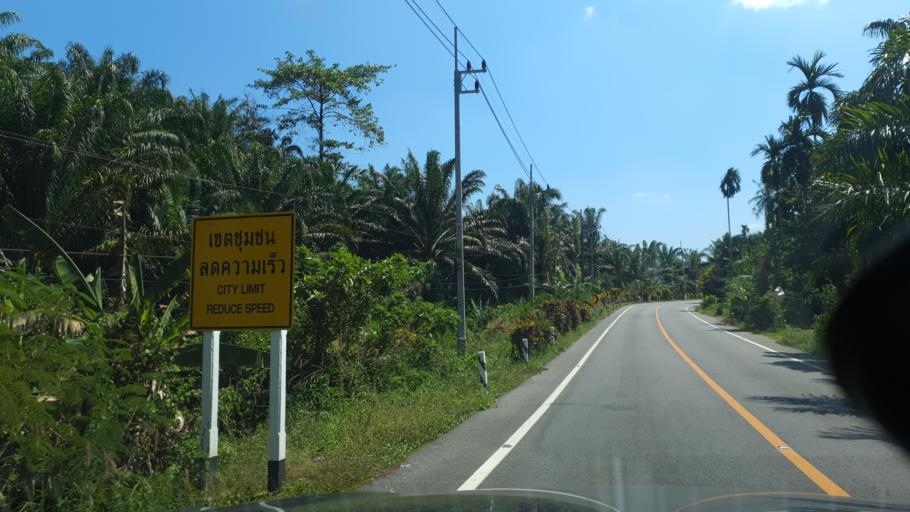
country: TH
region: Krabi
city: Khlong Thom
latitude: 7.9236
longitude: 99.2441
